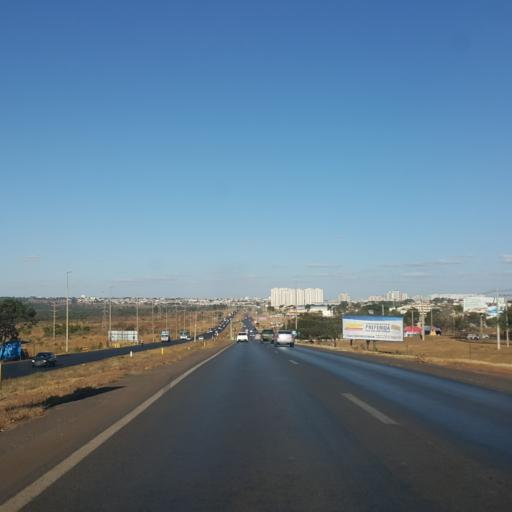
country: BR
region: Federal District
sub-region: Brasilia
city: Brasilia
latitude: -15.7885
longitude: -48.1127
